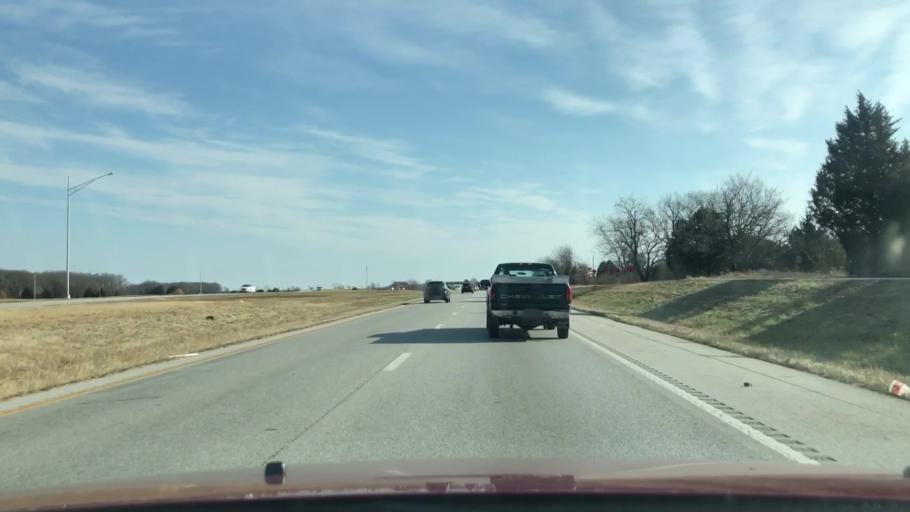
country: US
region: Missouri
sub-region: Webster County
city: Rogersville
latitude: 37.1180
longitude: -93.0962
